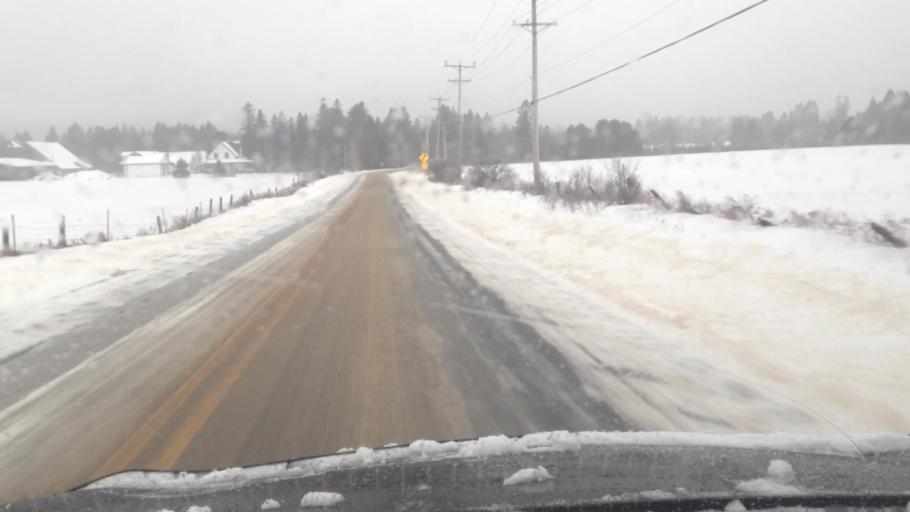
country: CA
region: Quebec
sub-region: Laurentides
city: Mont-Tremblant
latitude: 45.9897
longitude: -74.6169
